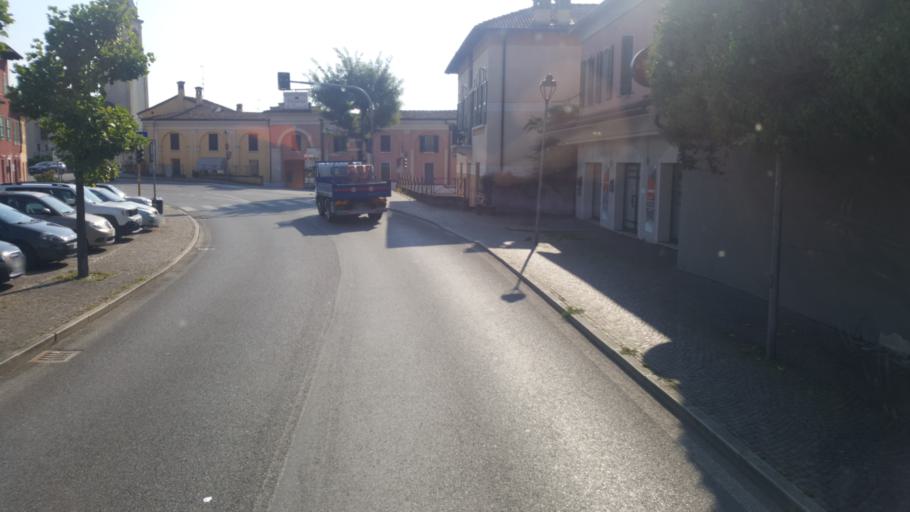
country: IT
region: Lombardy
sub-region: Provincia di Brescia
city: Pontevico
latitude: 45.2711
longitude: 10.0914
